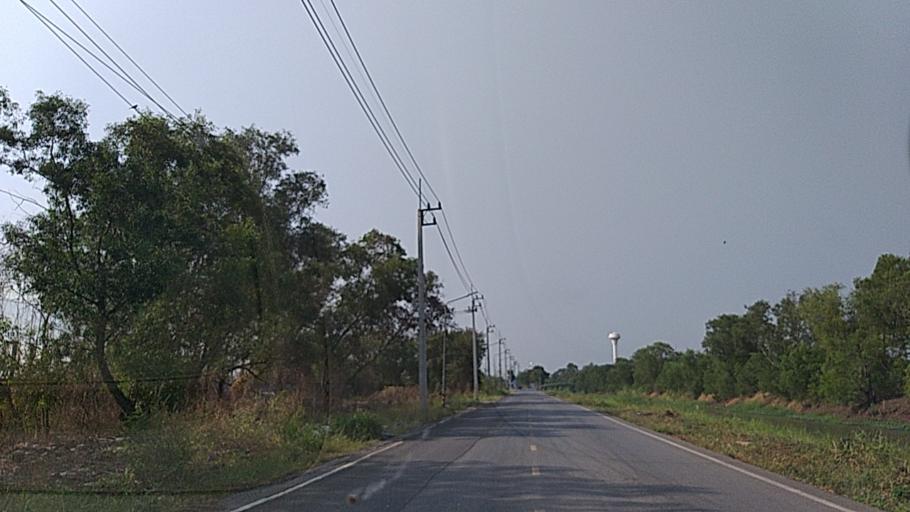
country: TH
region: Pathum Thani
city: Thanyaburi
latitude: 13.9958
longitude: 100.7070
